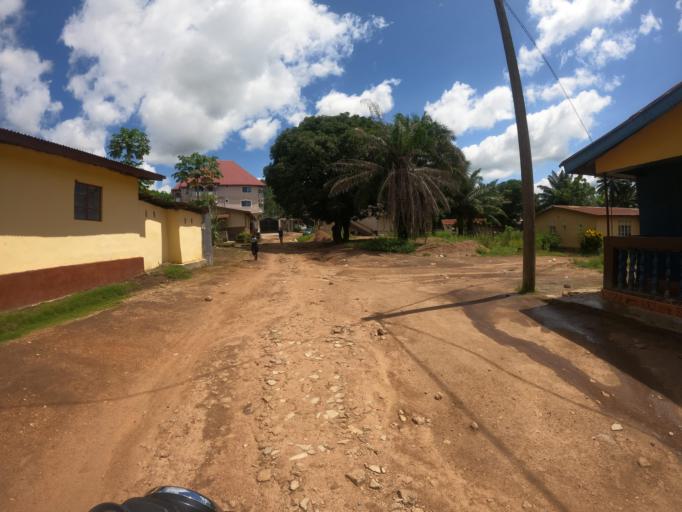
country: SL
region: Northern Province
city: Makeni
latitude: 8.8881
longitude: -12.0664
